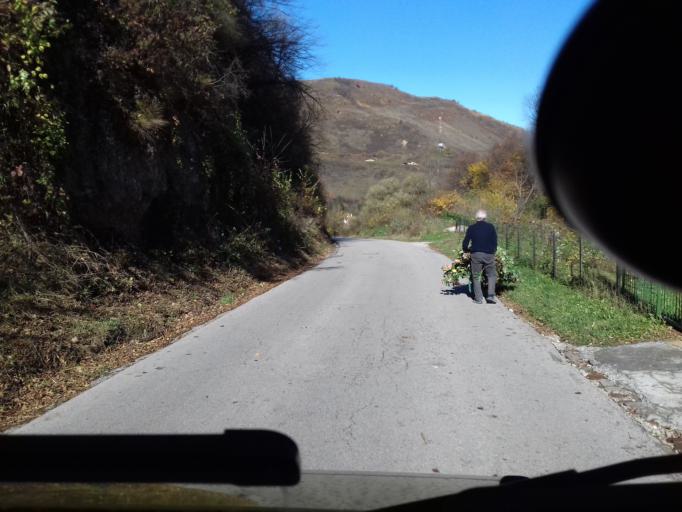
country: BA
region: Federation of Bosnia and Herzegovina
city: Zenica
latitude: 44.1807
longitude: 17.9025
